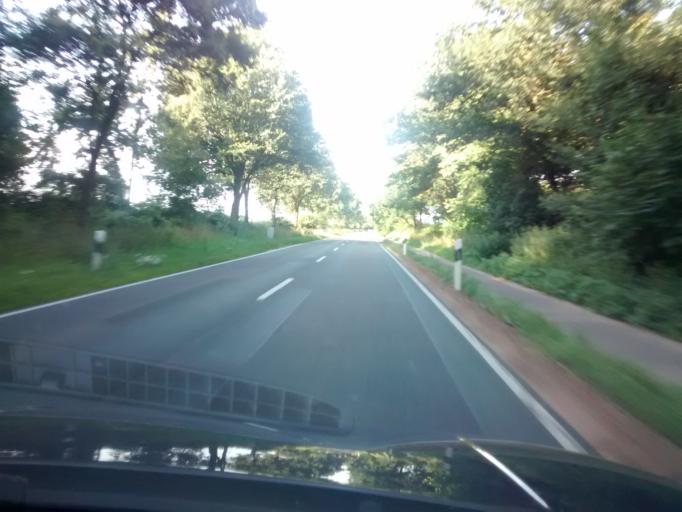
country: DE
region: Lower Saxony
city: Meppen
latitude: 52.6776
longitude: 7.2390
